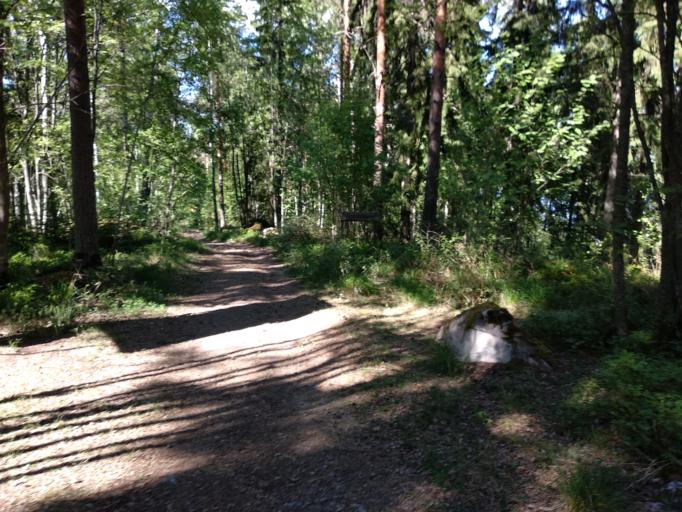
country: FI
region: Pirkanmaa
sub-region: Tampere
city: Kangasala
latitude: 61.4382
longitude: 24.1273
